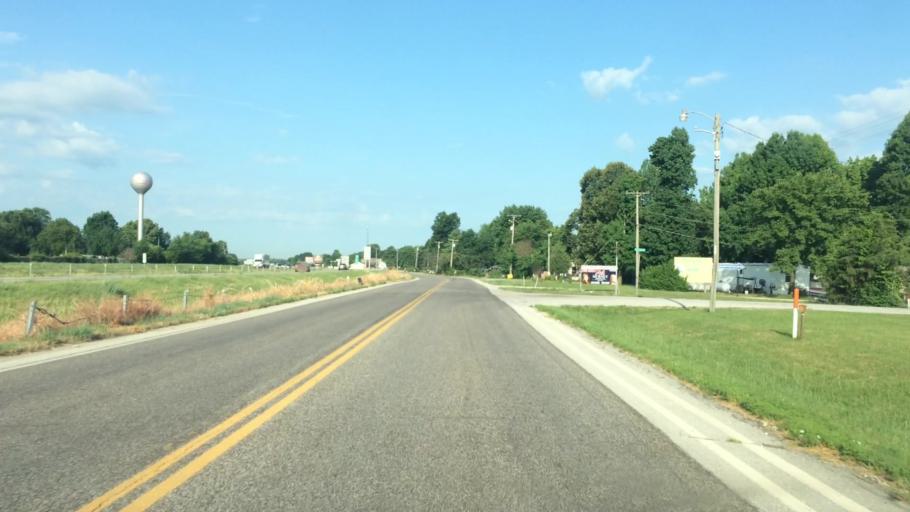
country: US
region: Missouri
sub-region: Greene County
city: Strafford
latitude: 37.2726
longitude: -93.1221
